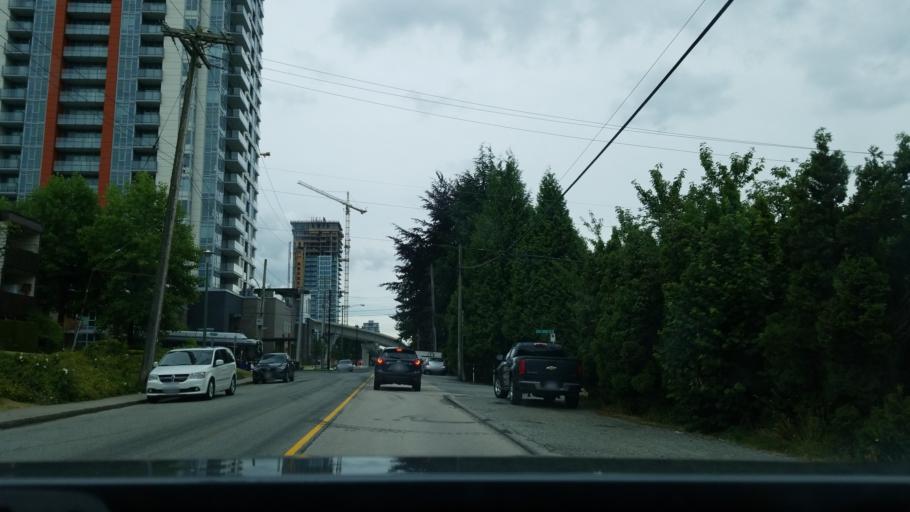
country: CA
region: British Columbia
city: Port Moody
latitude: 49.2610
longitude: -122.8931
